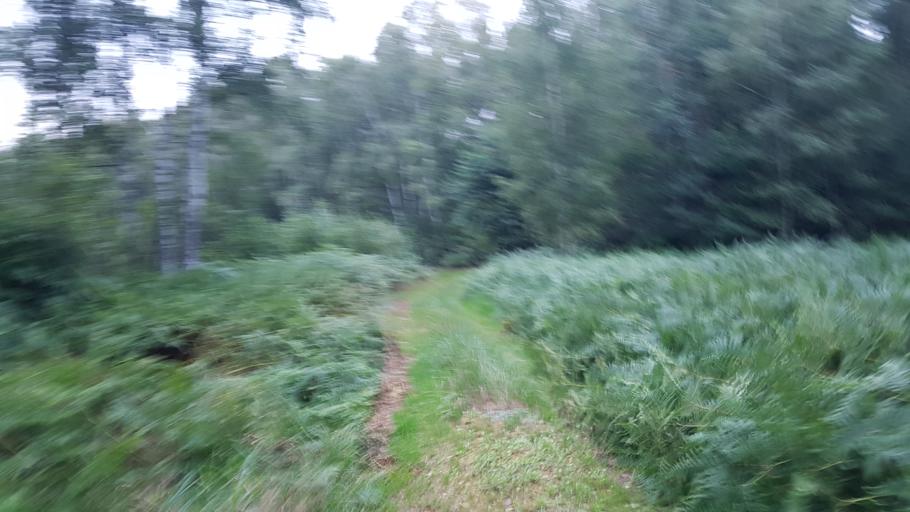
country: DE
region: Brandenburg
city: Schonborn
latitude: 51.5645
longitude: 13.4754
